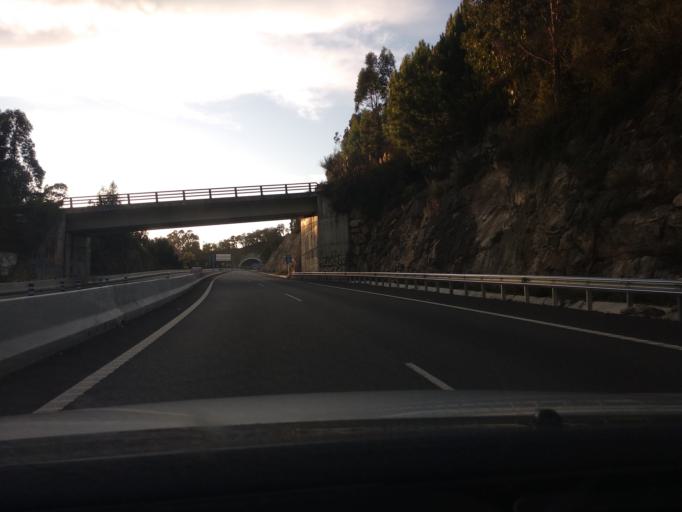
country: ES
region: Galicia
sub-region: Provincia de Pontevedra
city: Redondela
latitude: 42.2927
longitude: -8.6643
